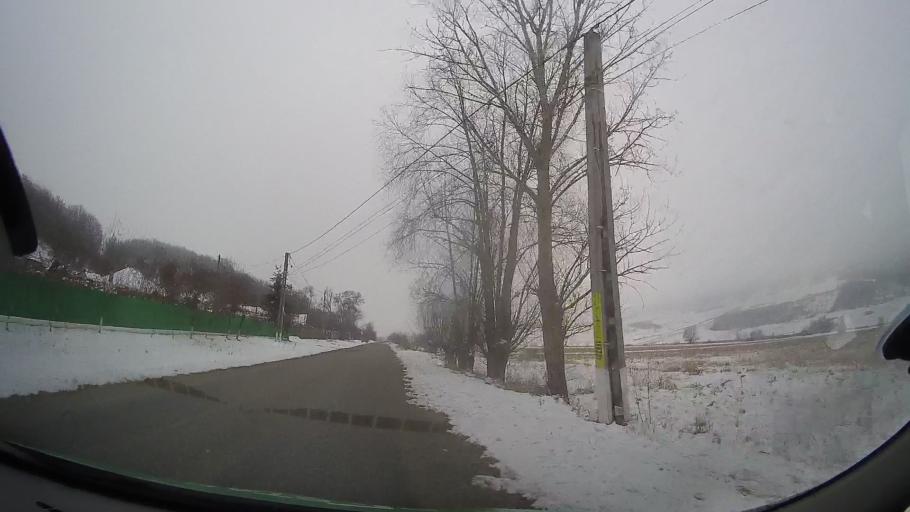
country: RO
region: Bacau
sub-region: Comuna Vultureni
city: Vultureni
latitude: 46.3417
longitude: 27.2909
